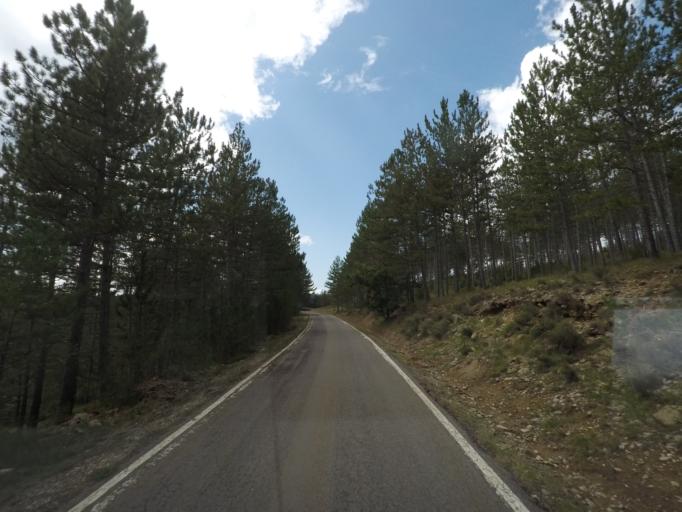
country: ES
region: Aragon
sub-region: Provincia de Huesca
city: Fiscal
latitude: 42.4085
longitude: -0.1519
